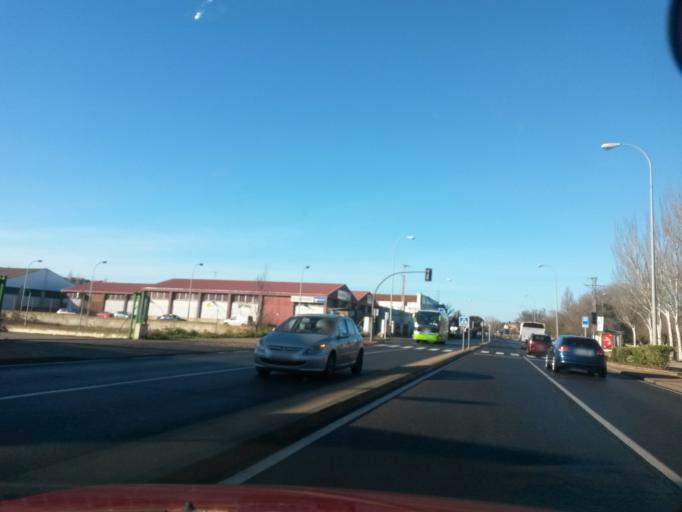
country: ES
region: Castille and Leon
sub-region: Provincia de Salamanca
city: Salamanca
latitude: 40.9549
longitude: -5.6862
